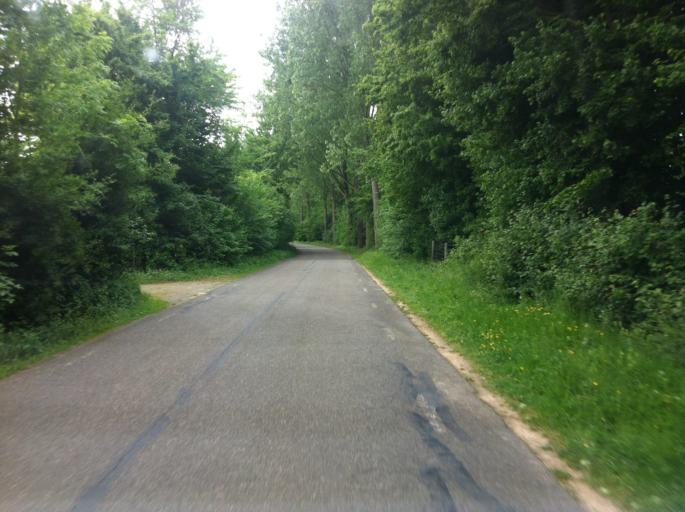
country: NL
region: Limburg
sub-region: Gemeente Roermond
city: Roermond
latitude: 51.2059
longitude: 5.9619
